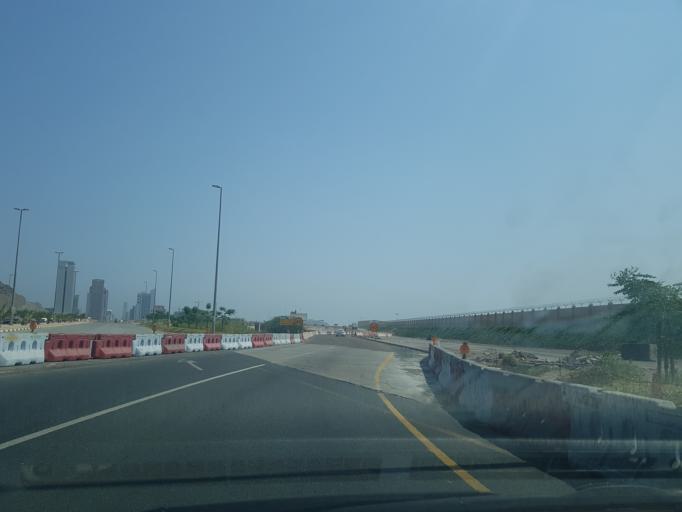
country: AE
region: Al Fujayrah
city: Al Fujayrah
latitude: 25.1224
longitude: 56.3062
